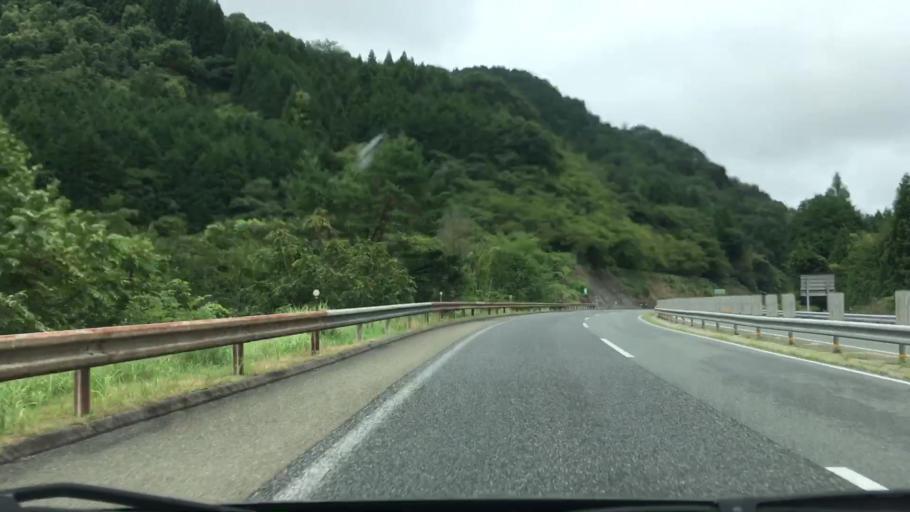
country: JP
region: Hiroshima
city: Shobara
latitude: 34.8443
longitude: 133.0878
